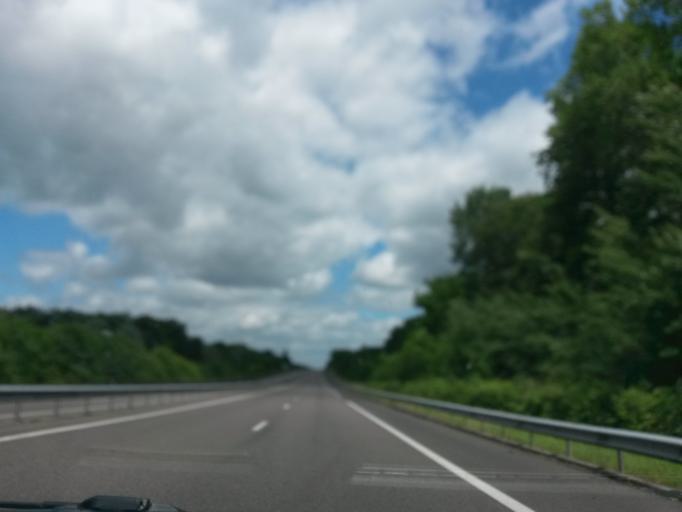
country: FR
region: Bourgogne
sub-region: Departement de la Nievre
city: Cosne-Cours-sur-Loire
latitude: 47.3638
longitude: 2.9235
